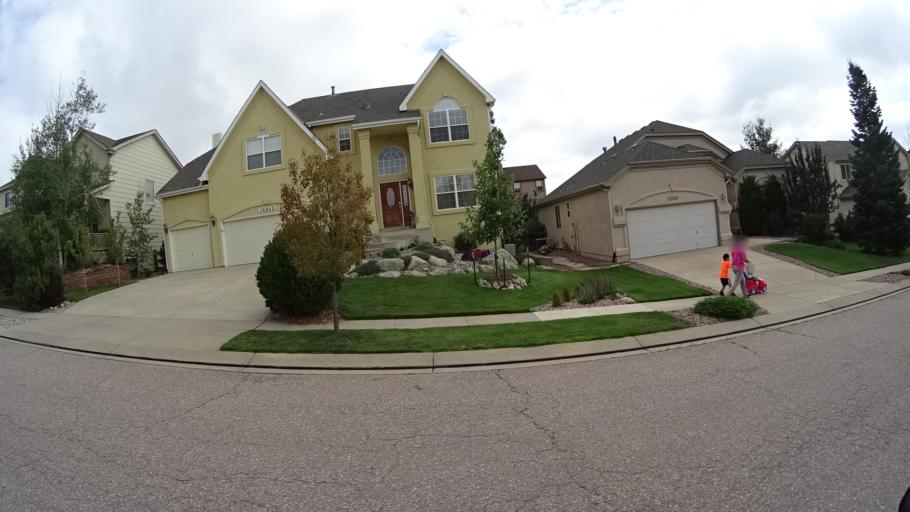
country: US
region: Colorado
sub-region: El Paso County
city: Gleneagle
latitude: 39.0137
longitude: -104.8056
